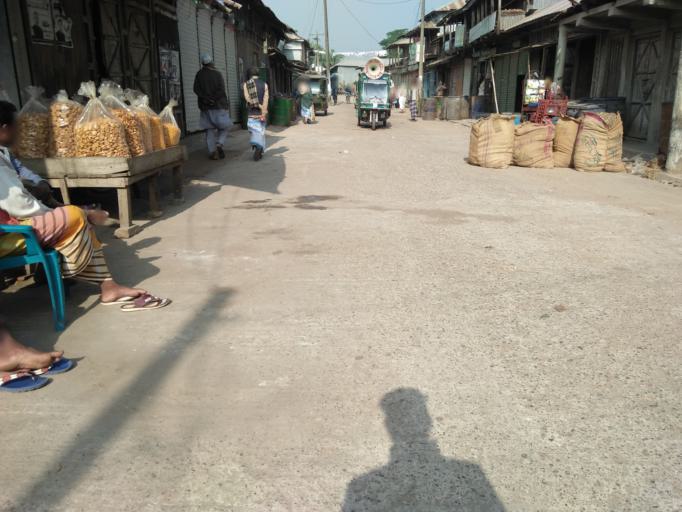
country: BD
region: Khulna
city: Uttar Char Fasson
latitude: 22.1923
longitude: 90.6737
